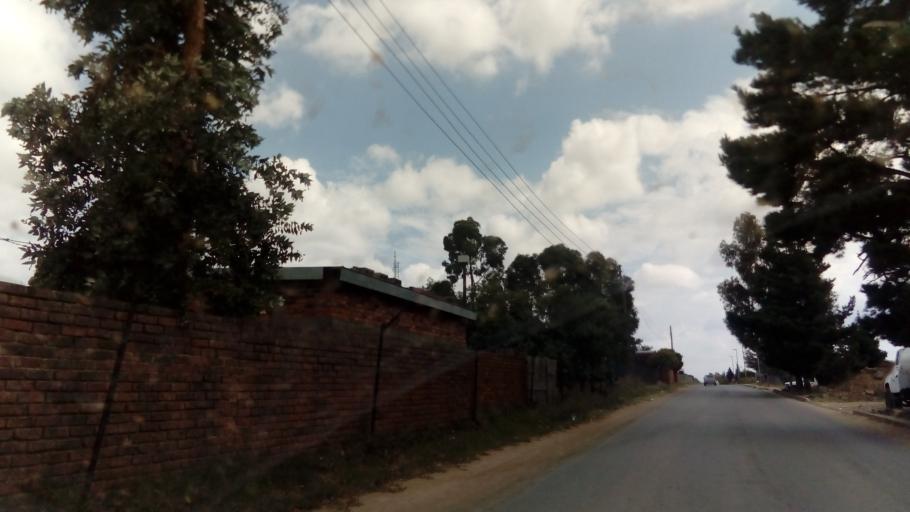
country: LS
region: Maseru
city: Maseru
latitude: -29.3758
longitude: 27.5312
